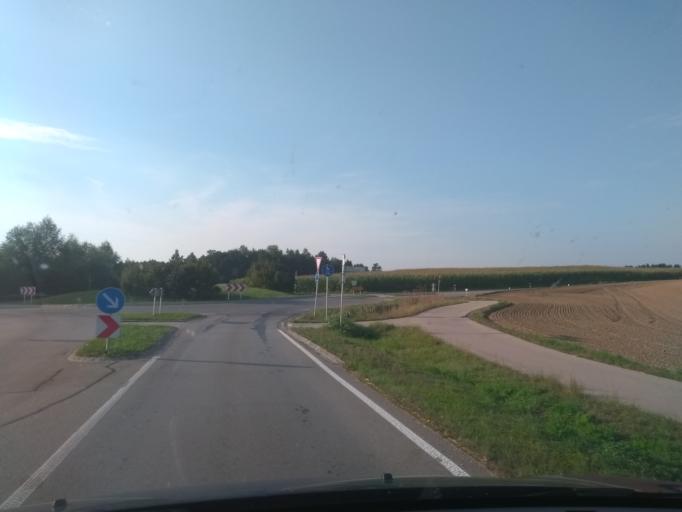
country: DE
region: Bavaria
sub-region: Upper Bavaria
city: Schwabhausen
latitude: 48.3049
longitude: 11.3938
